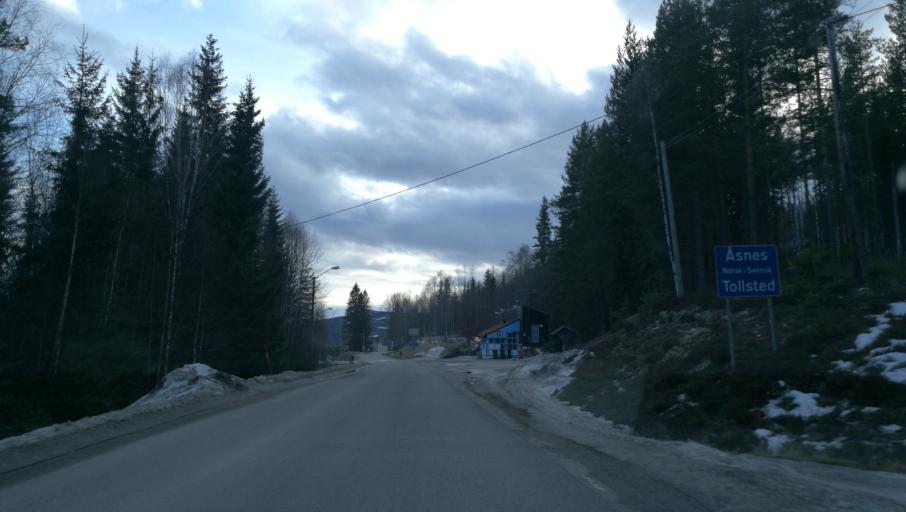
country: NO
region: Hedmark
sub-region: Asnes
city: Flisa
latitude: 60.6909
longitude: 12.4567
